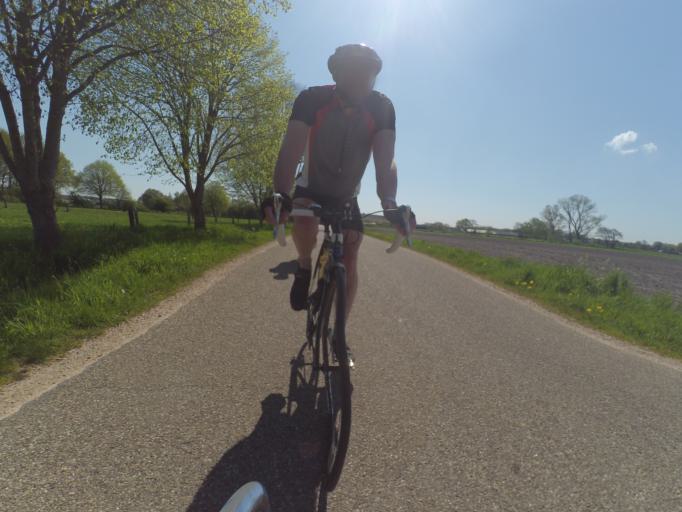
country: NL
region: Gelderland
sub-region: Gemeente Apeldoorn
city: Uddel
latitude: 52.2659
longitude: 5.7666
